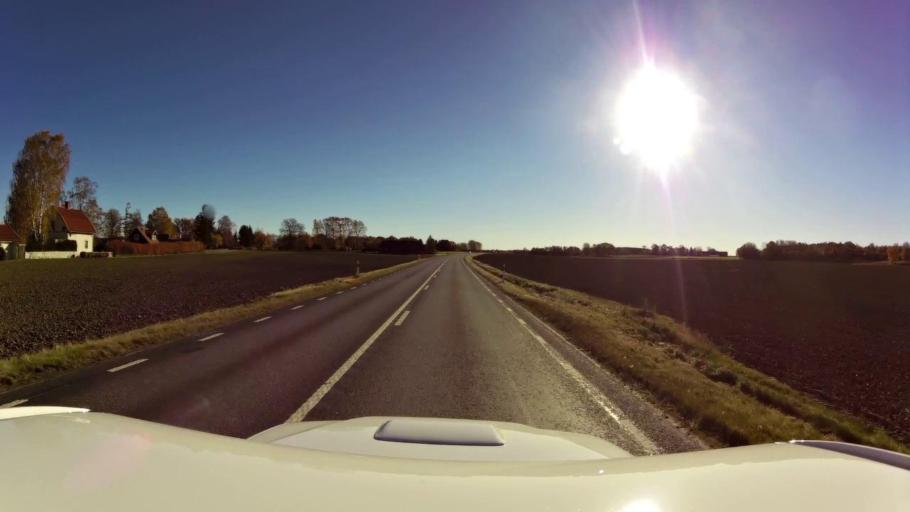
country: SE
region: OEstergoetland
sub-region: Linkopings Kommun
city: Ljungsbro
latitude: 58.5272
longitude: 15.4118
